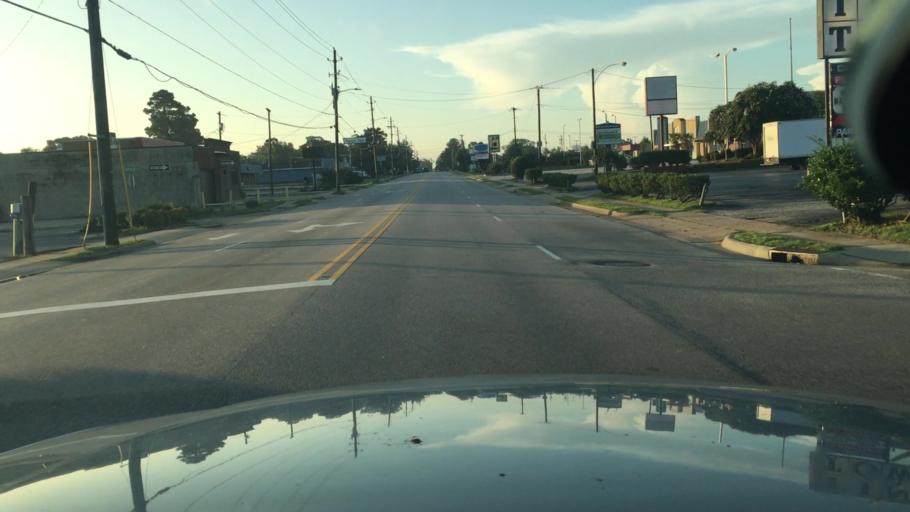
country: US
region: North Carolina
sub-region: Cumberland County
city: Fayetteville
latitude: 35.0730
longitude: -78.9277
